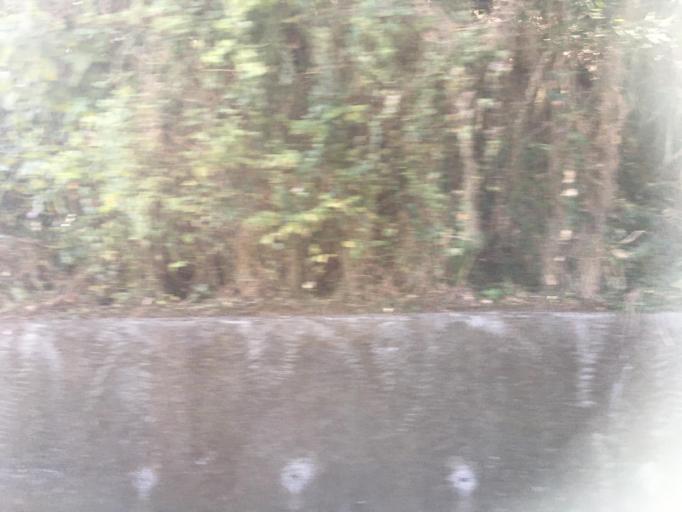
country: TW
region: Taiwan
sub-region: Chiayi
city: Jiayi Shi
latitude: 23.4082
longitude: 120.6544
